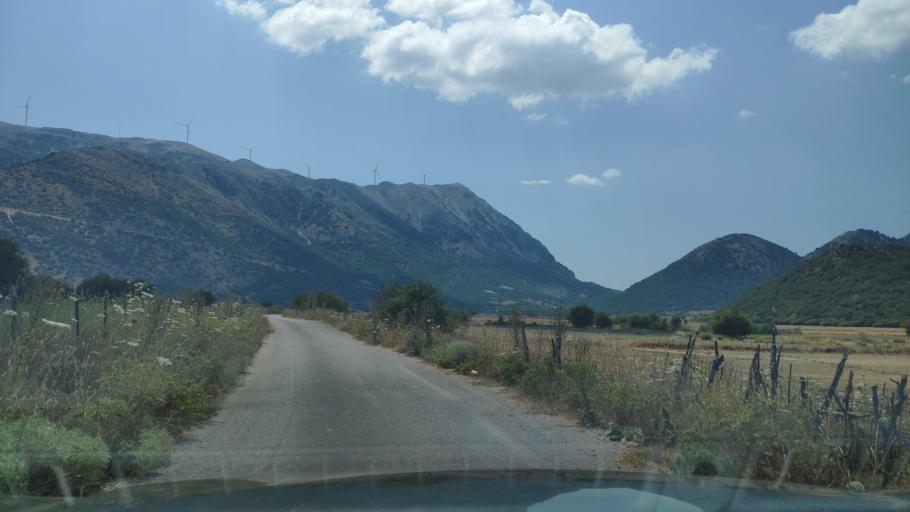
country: GR
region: West Greece
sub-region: Nomos Aitolias kai Akarnanias
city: Monastirakion
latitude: 38.7905
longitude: 20.9618
